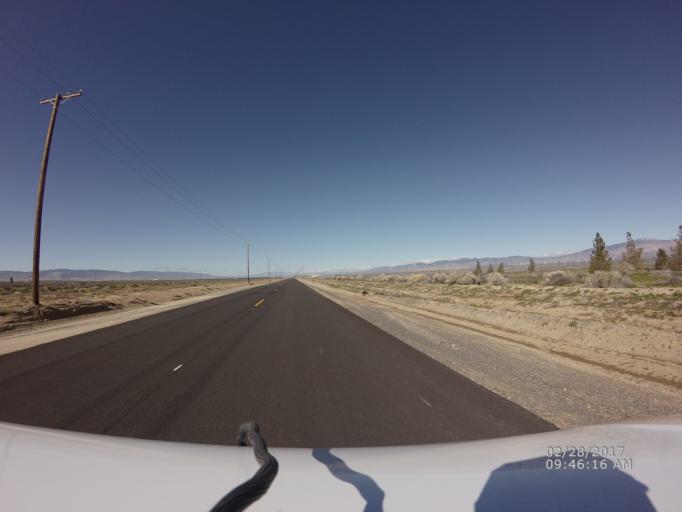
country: US
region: California
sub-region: Kern County
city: Rosamond
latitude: 34.8195
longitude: -118.3576
